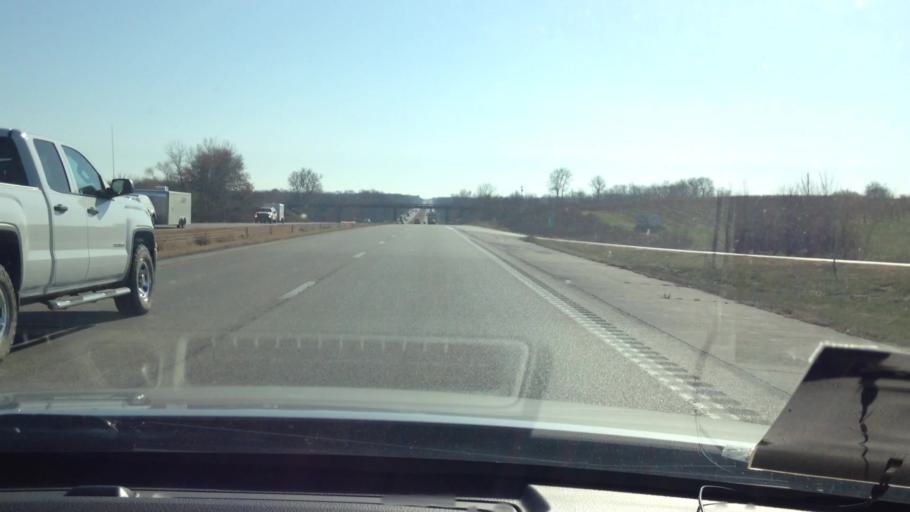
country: US
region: Missouri
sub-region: Platte County
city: Platte City
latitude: 39.4742
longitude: -94.7875
